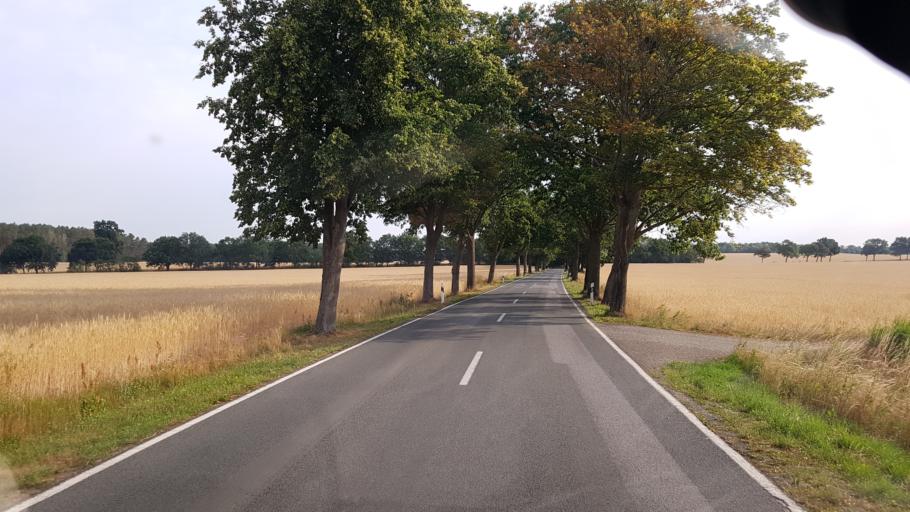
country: DE
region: Brandenburg
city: Golssen
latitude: 51.9625
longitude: 13.5432
